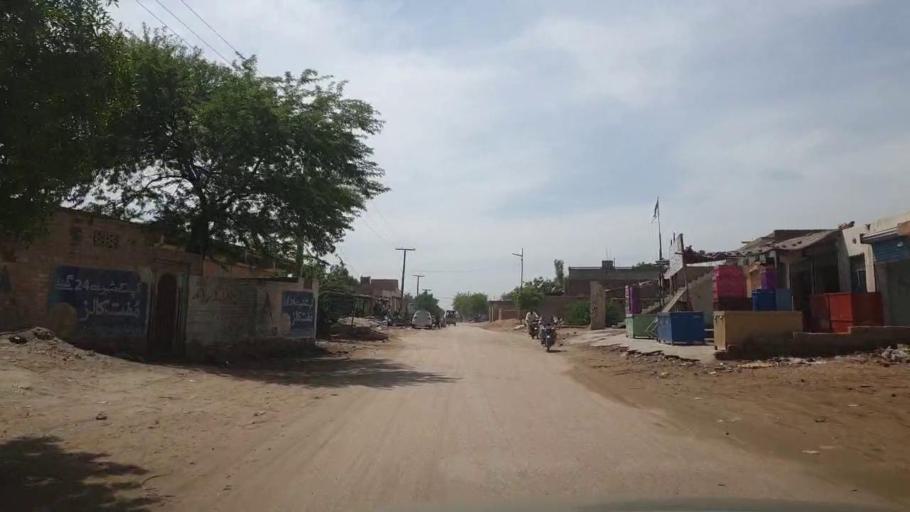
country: PK
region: Sindh
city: Kot Diji
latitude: 27.1583
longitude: 68.9592
